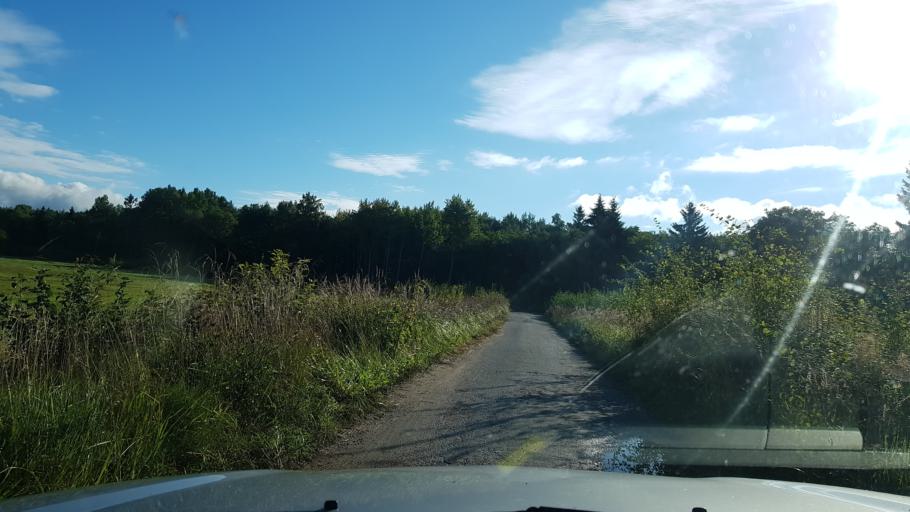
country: EE
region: Harju
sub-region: Rae vald
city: Jueri
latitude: 59.3389
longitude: 24.8933
